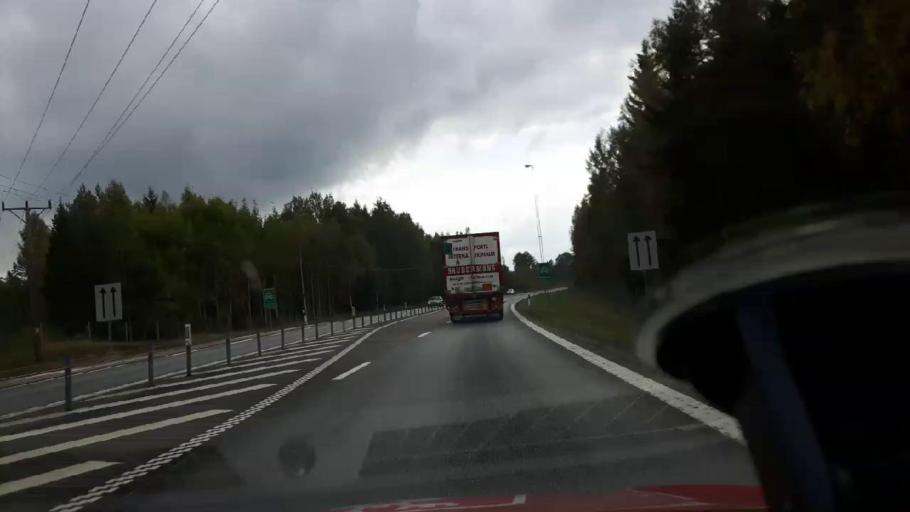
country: SE
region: Gaevleborg
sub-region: Gavle Kommun
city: Norrsundet
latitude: 60.9597
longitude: 17.0344
